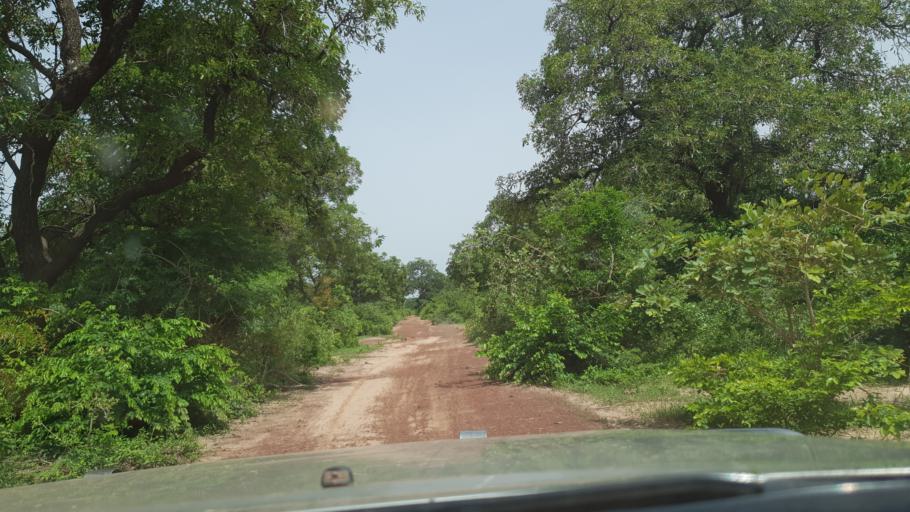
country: ML
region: Koulikoro
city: Koulikoro
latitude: 12.6640
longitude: -7.2126
